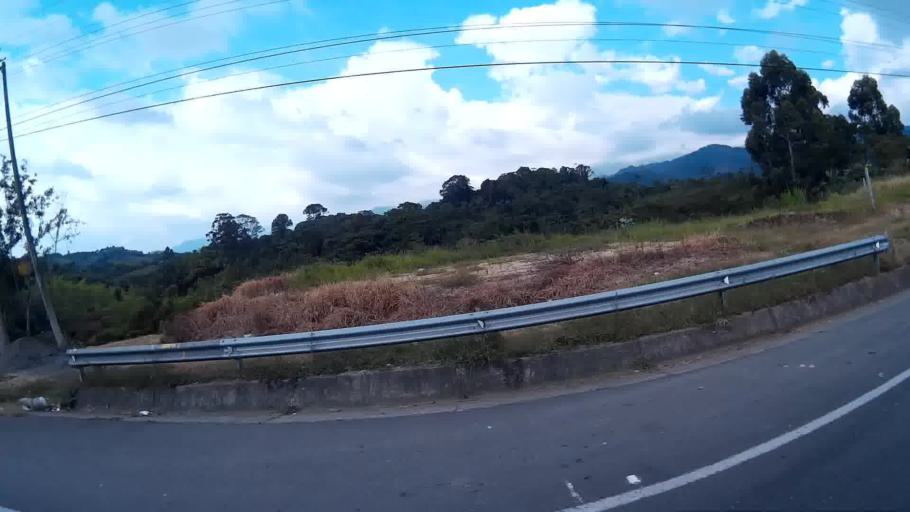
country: CO
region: Quindio
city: Circasia
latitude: 4.5868
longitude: -75.6430
